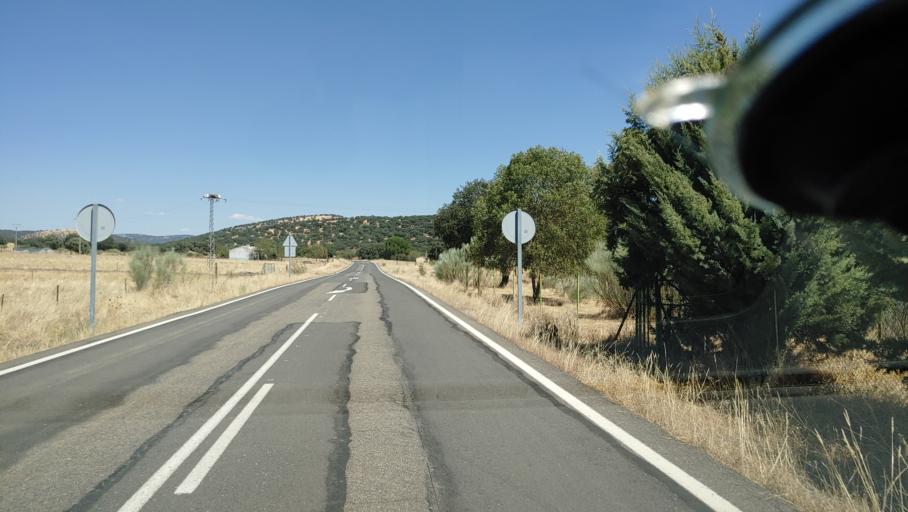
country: ES
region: Castille-La Mancha
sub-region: Provincia de Ciudad Real
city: Alamillo
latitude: 38.7572
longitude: -4.7015
